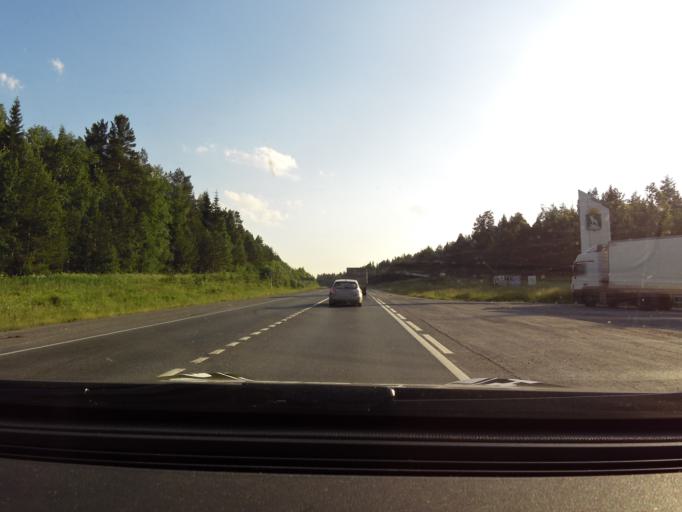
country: RU
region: Sverdlovsk
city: Druzhinino
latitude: 56.8208
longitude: 59.5696
